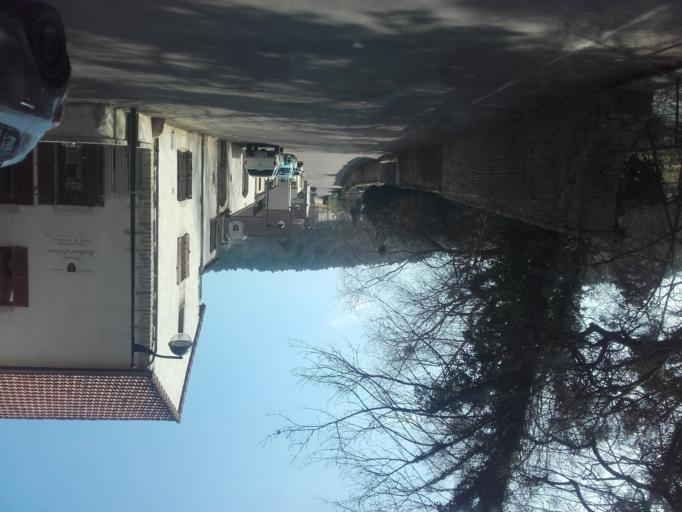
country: FR
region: Bourgogne
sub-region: Departement de la Cote-d'Or
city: Savigny-les-Beaune
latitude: 47.0625
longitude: 4.8162
